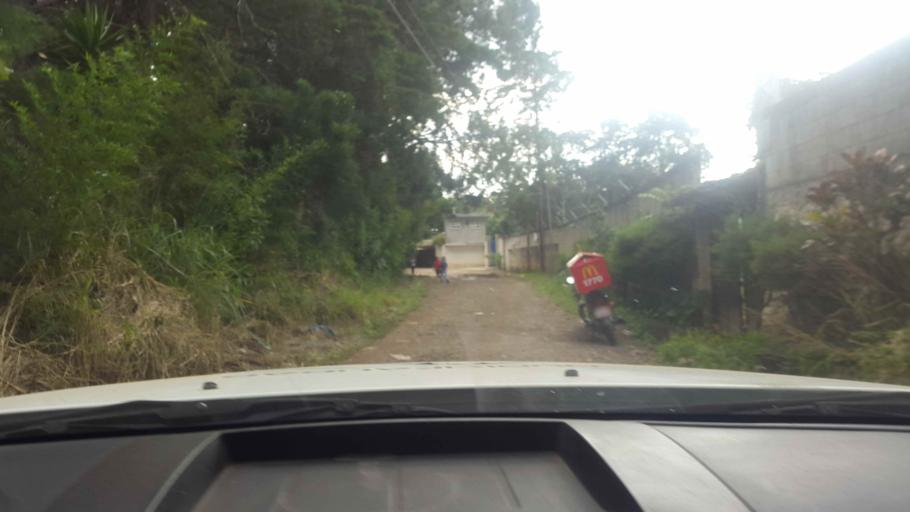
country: GT
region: Guatemala
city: Petapa
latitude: 14.5069
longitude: -90.5388
